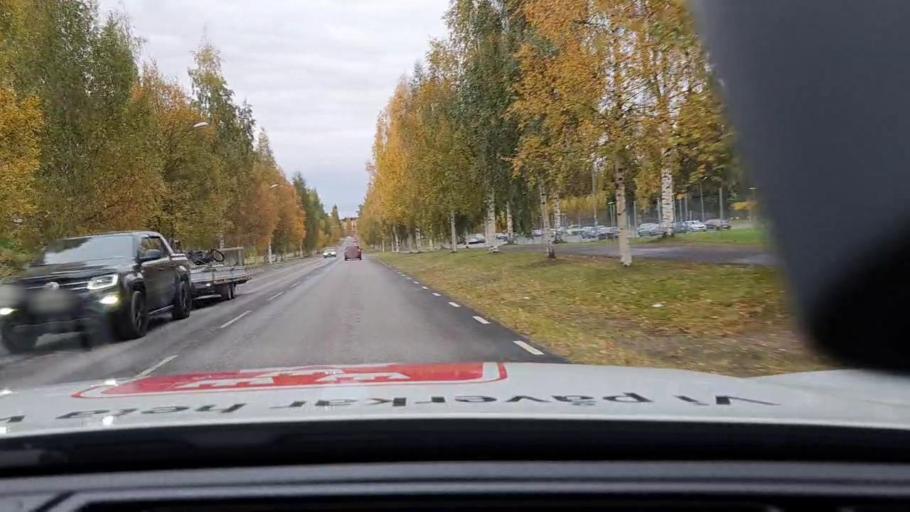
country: SE
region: Norrbotten
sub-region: Bodens Kommun
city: Boden
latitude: 65.8176
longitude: 21.6672
